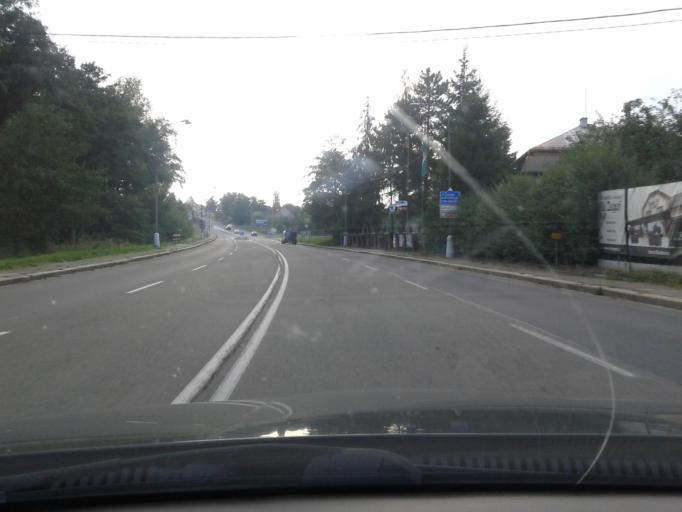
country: CZ
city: Petrvald
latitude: 49.8296
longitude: 18.3785
